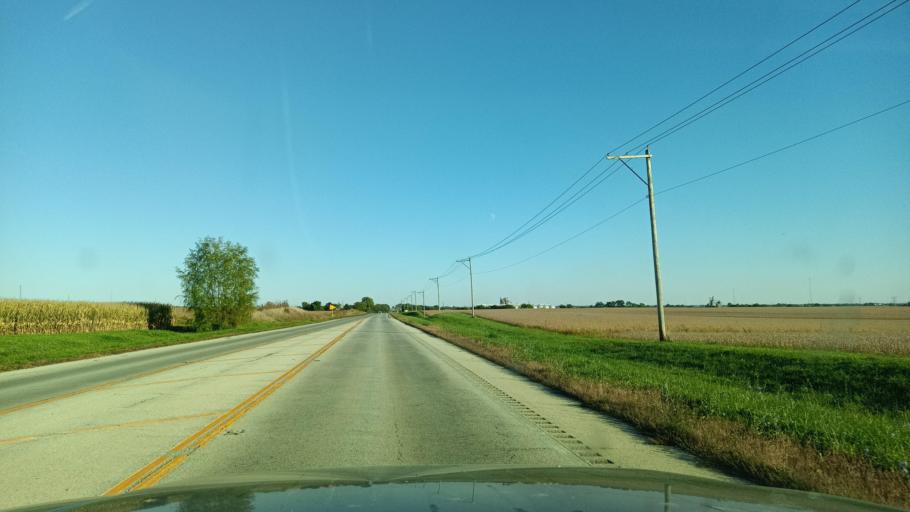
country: US
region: Illinois
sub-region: Champaign County
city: Lake of the Woods
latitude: 40.1770
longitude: -88.3495
